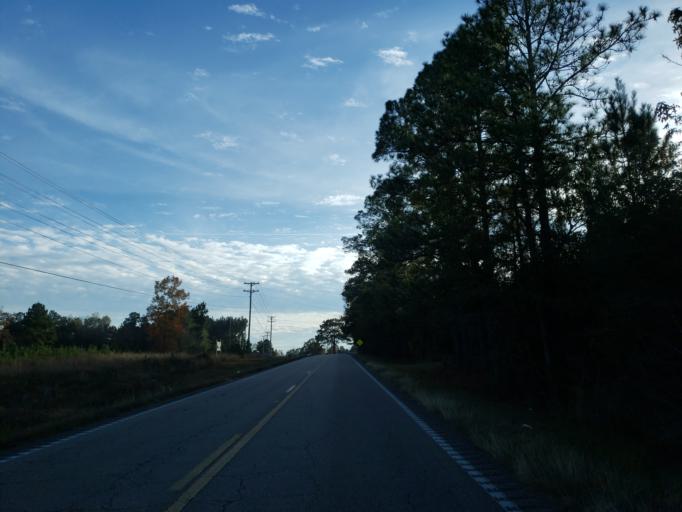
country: US
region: Mississippi
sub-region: Lamar County
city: West Hattiesburg
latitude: 31.2935
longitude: -89.4704
